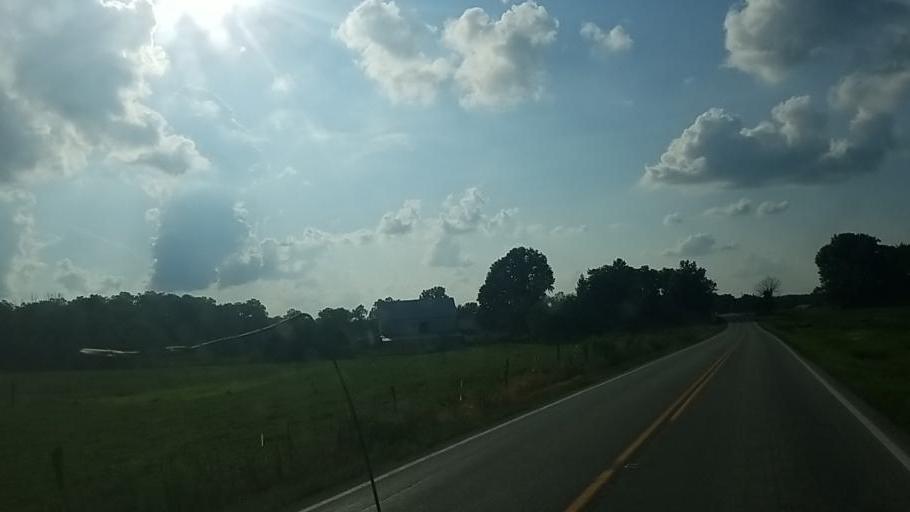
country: US
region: Ohio
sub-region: Wayne County
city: West Salem
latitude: 40.8813
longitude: -82.1130
